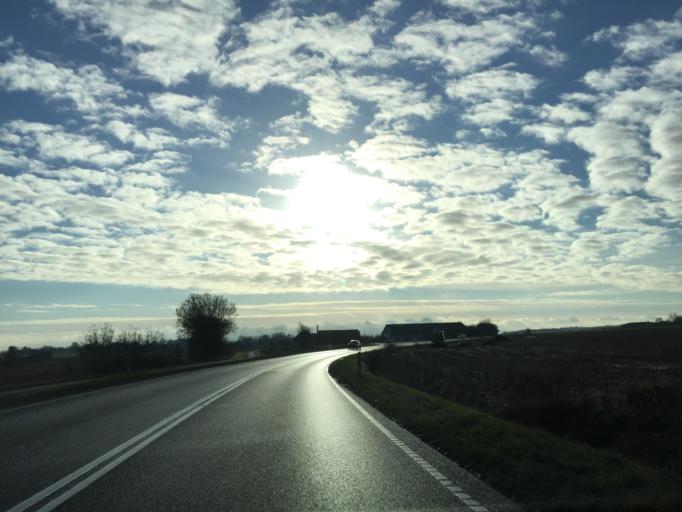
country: DK
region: Central Jutland
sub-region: Arhus Kommune
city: Sabro
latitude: 56.1975
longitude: 10.0141
